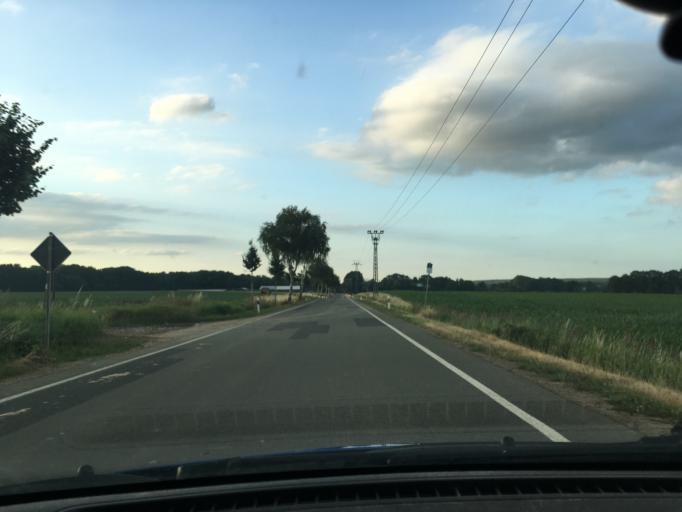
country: DE
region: Lower Saxony
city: Eyendorf
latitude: 53.1867
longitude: 10.1868
